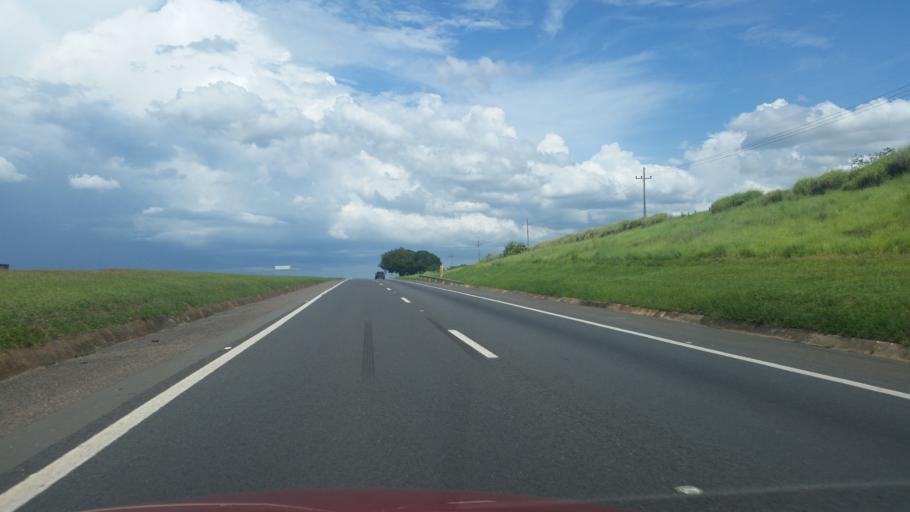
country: BR
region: Sao Paulo
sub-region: Tatui
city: Tatui
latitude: -23.2561
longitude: -47.9067
